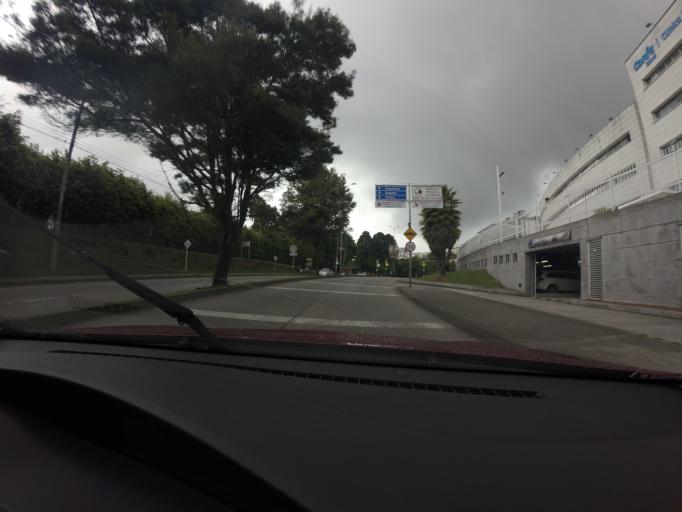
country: CO
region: Caldas
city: Villamaria
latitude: 5.0352
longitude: -75.4684
